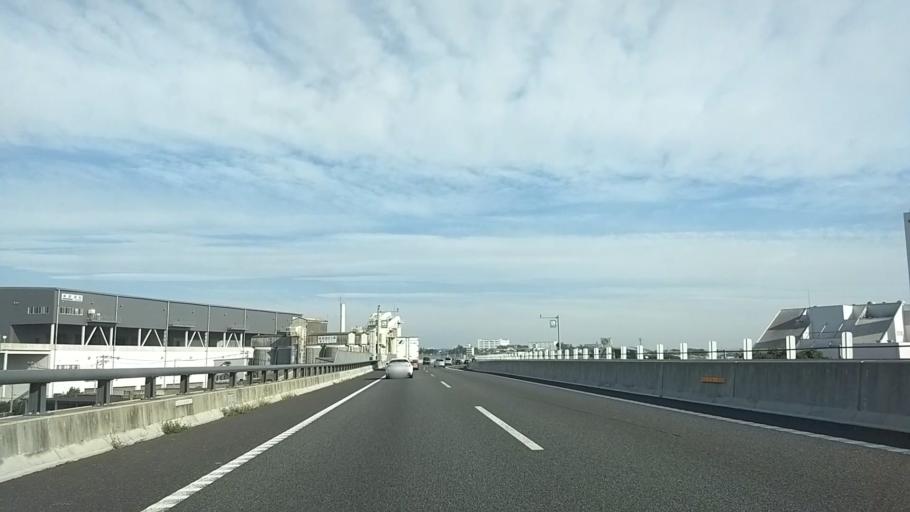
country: JP
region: Kanagawa
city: Atsugi
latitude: 35.4551
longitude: 139.3731
